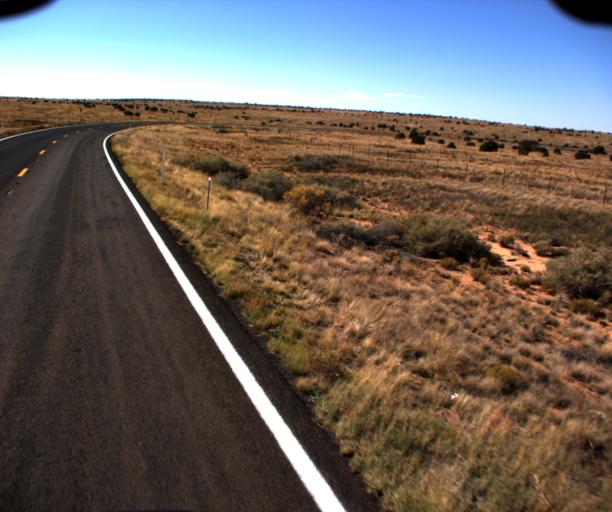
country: US
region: Arizona
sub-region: Coconino County
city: Tuba City
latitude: 35.9075
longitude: -110.8782
